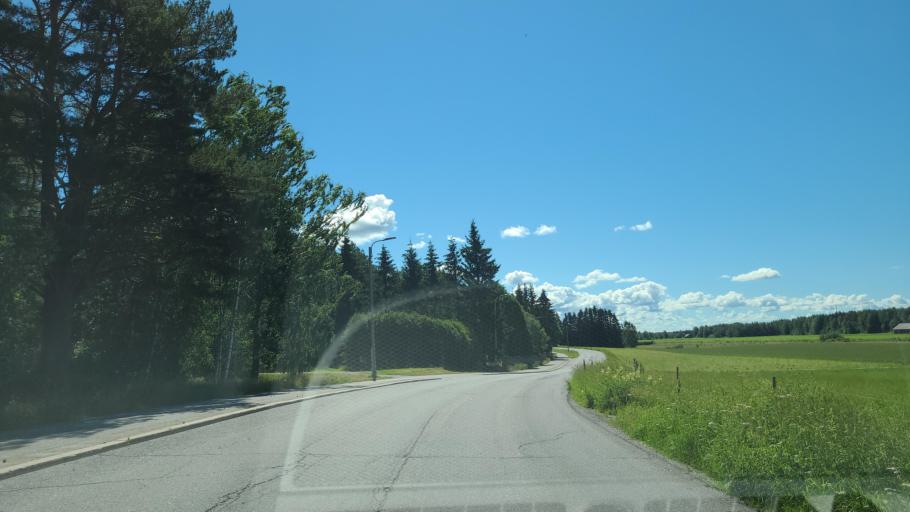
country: FI
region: Ostrobothnia
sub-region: Vaasa
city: Ristinummi
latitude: 63.0649
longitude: 21.7253
